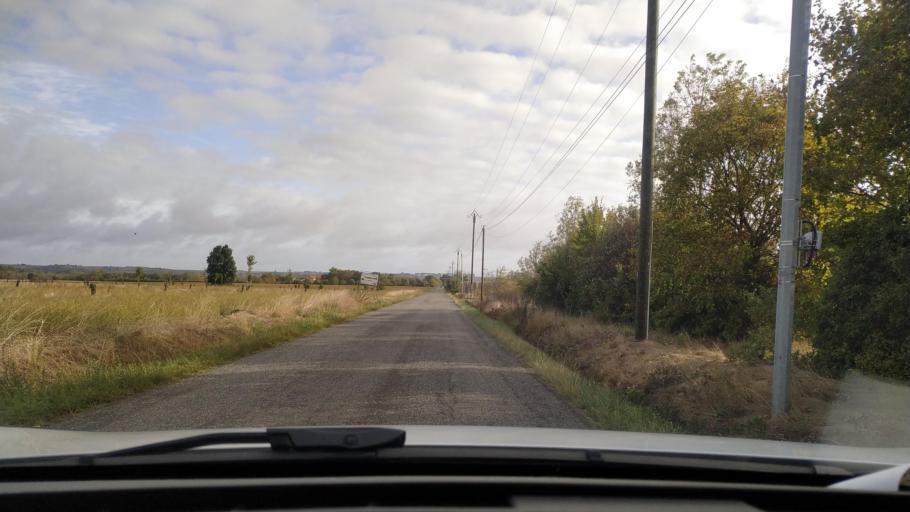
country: FR
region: Midi-Pyrenees
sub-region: Departement de la Haute-Garonne
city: Cintegabelle
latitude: 43.2845
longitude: 1.5112
